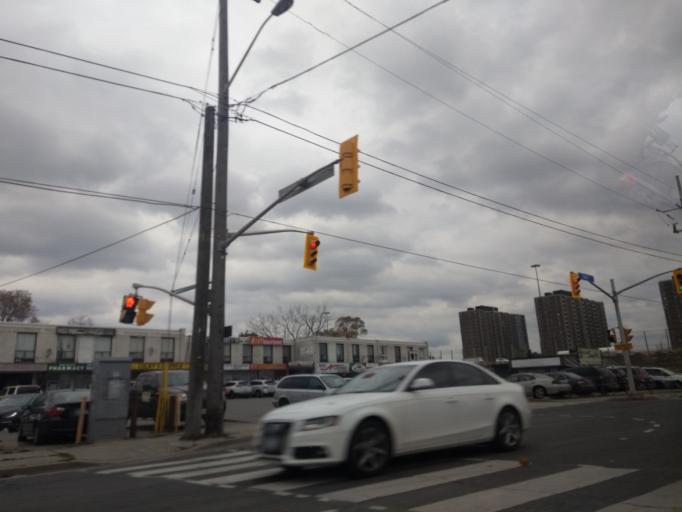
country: CA
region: Ontario
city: Concord
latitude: 43.7192
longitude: -79.5081
